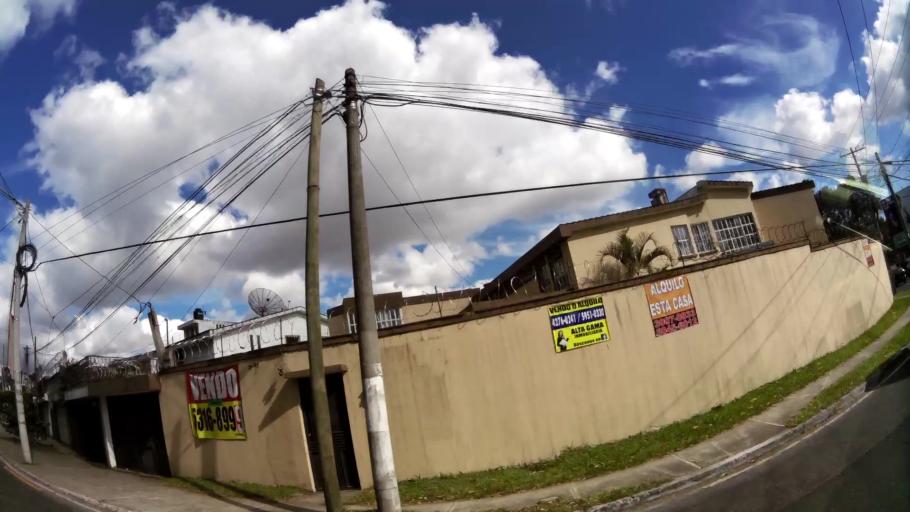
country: GT
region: Guatemala
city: Mixco
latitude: 14.5979
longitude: -90.5644
